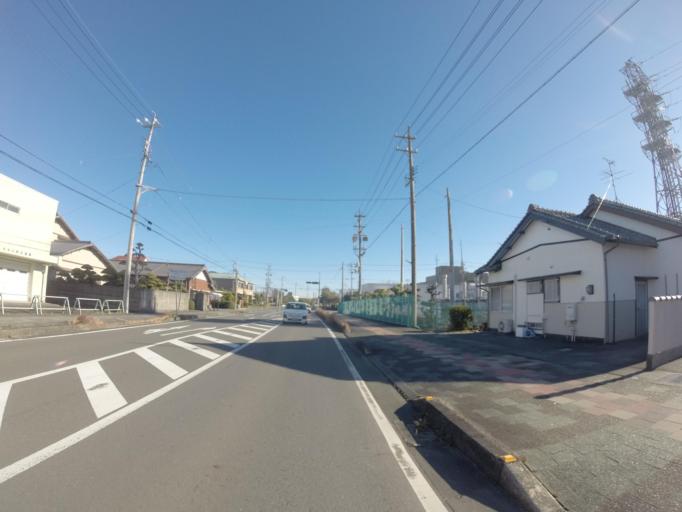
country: JP
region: Shizuoka
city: Fujieda
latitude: 34.8049
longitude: 138.2837
